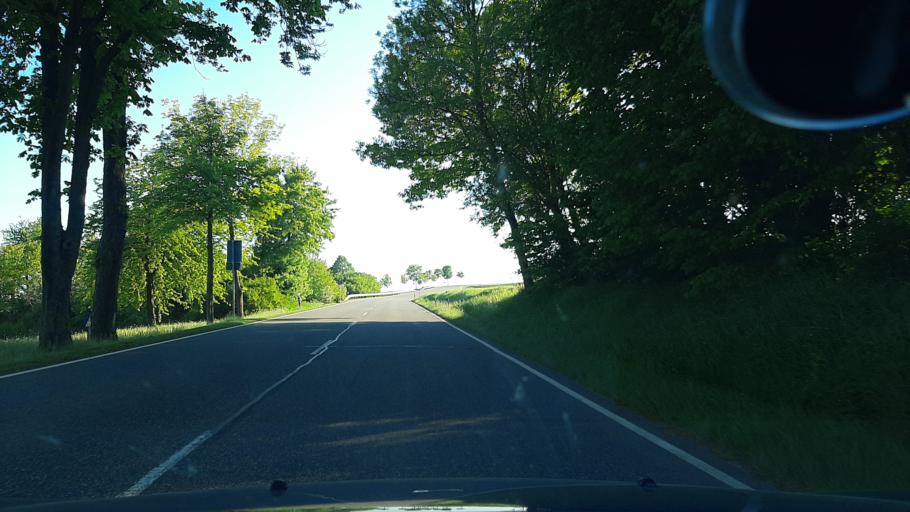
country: DE
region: Rheinland-Pfalz
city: Ohlenhard
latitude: 50.4893
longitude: 6.7264
